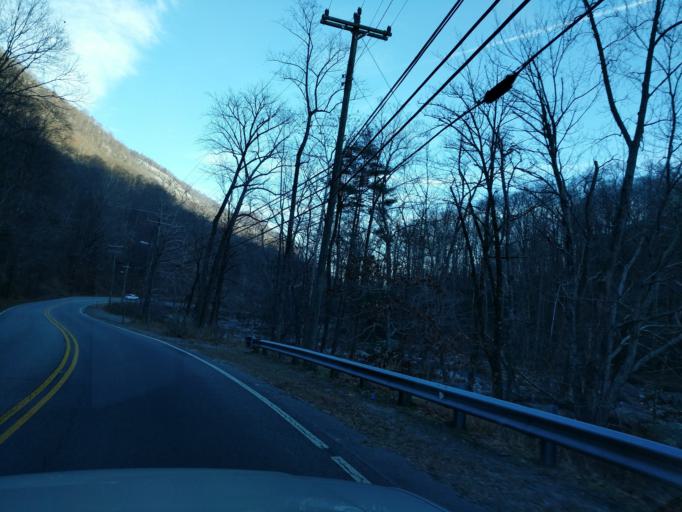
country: US
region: North Carolina
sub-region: Rutherford County
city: Lake Lure
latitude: 35.4455
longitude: -82.2737
